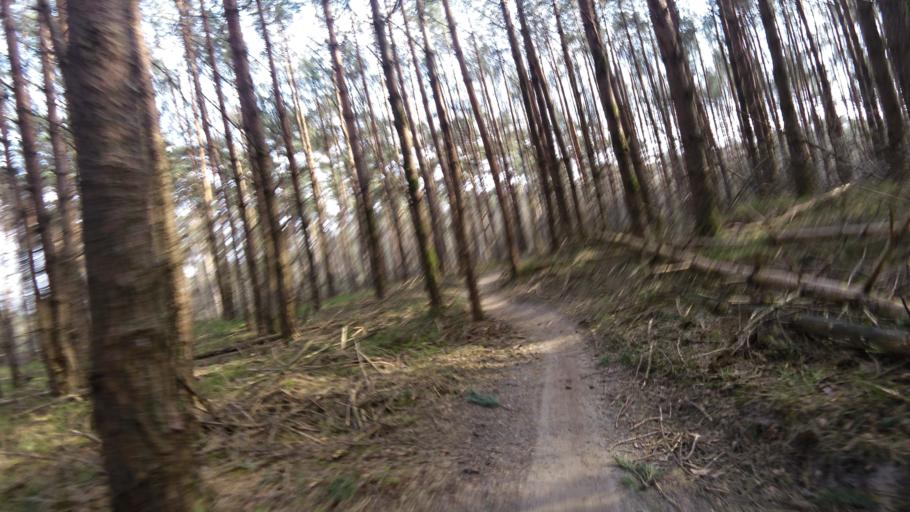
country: NL
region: Gelderland
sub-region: Gemeente Ede
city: Otterlo
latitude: 52.0868
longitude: 5.7419
